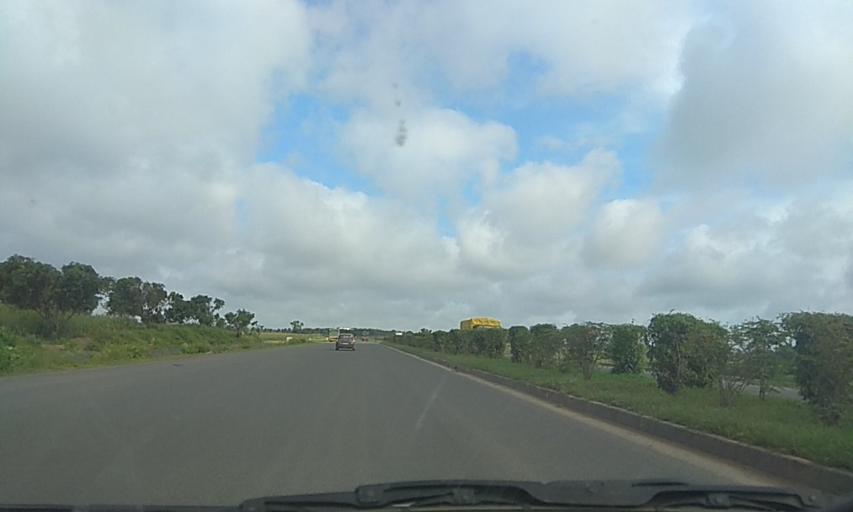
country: IN
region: Karnataka
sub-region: Haveri
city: Shiggaon
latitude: 15.0004
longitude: 75.2074
